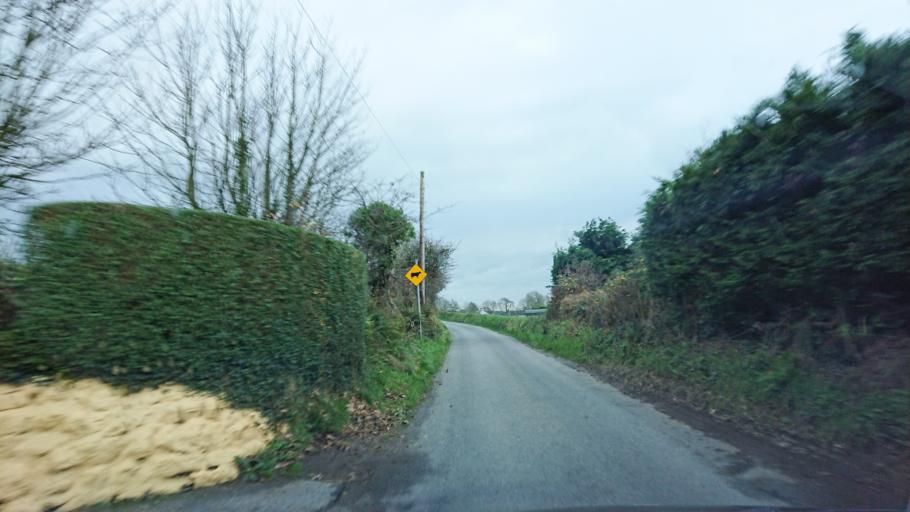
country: IE
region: Munster
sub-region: Waterford
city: Dunmore East
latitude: 52.2507
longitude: -7.0089
